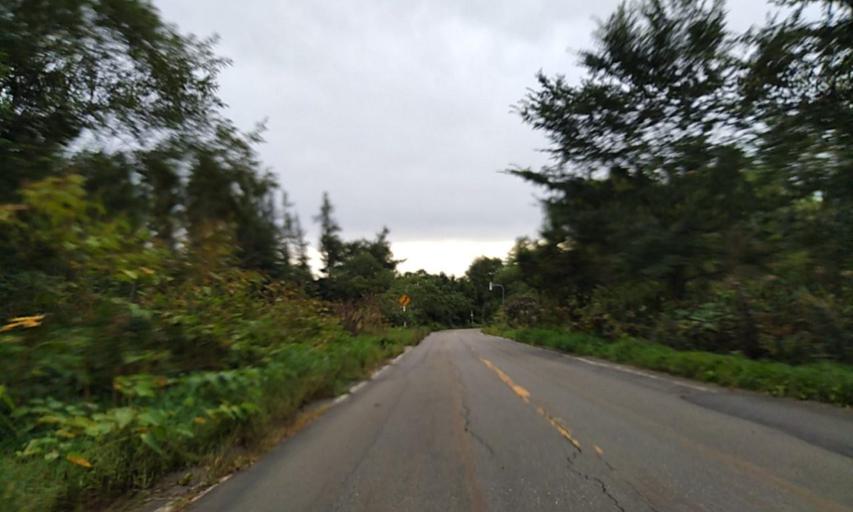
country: JP
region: Hokkaido
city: Obihiro
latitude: 42.6619
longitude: 143.0751
